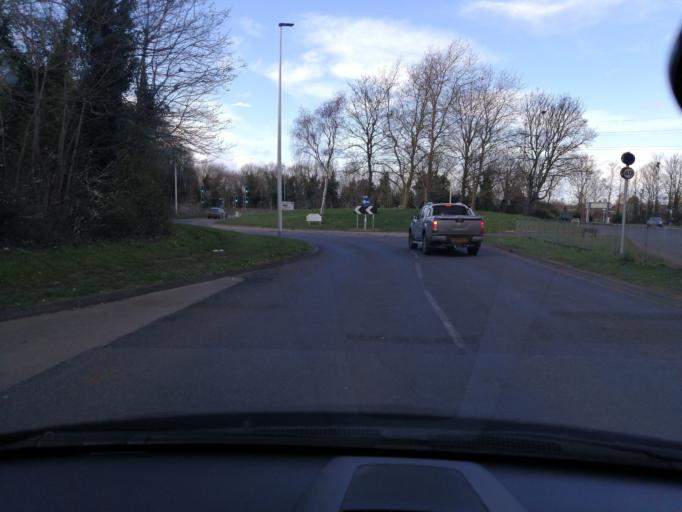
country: GB
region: England
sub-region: Peterborough
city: Marholm
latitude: 52.6033
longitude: -0.2761
